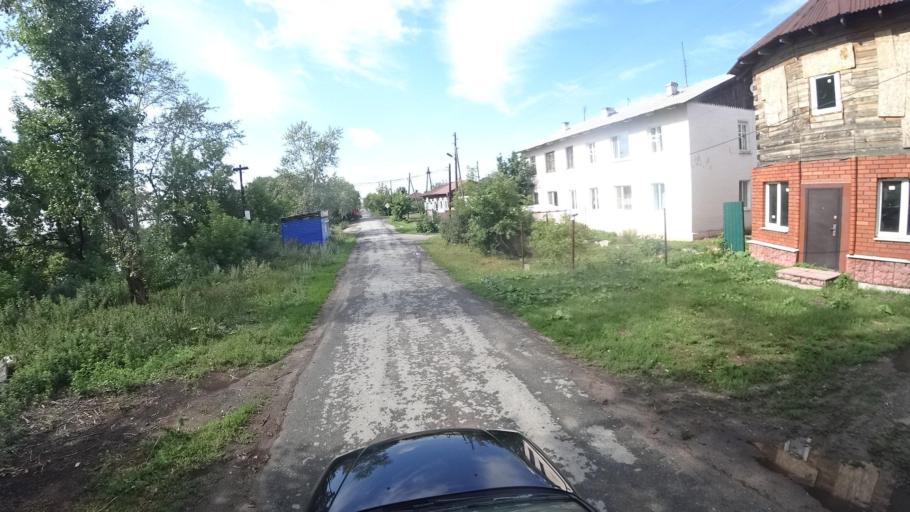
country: RU
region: Sverdlovsk
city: Kamyshlov
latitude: 56.8383
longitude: 62.7068
